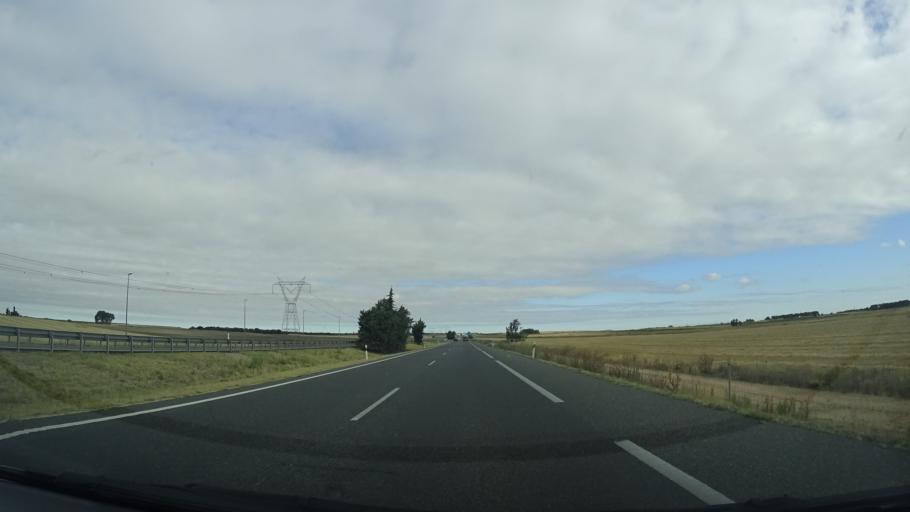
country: ES
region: Castille and Leon
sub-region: Provincia de Avila
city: Palacios de Goda
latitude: 41.1330
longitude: -4.7764
